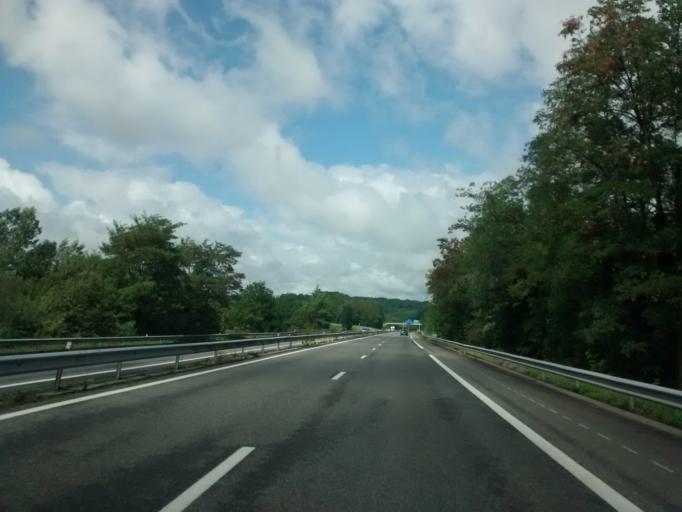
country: FR
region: Aquitaine
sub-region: Departement des Pyrenees-Atlantiques
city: Puyoo
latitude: 43.5109
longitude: -0.9175
